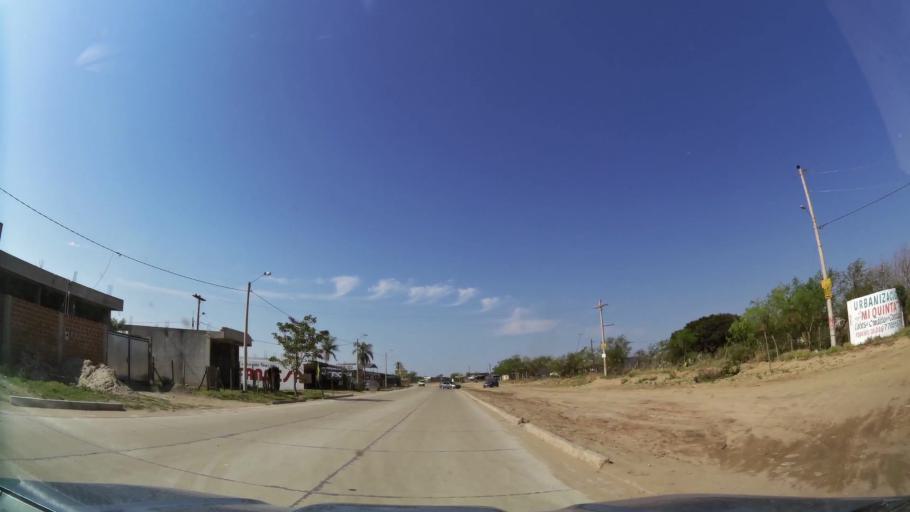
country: BO
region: Santa Cruz
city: Cotoca
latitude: -17.7220
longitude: -63.0776
